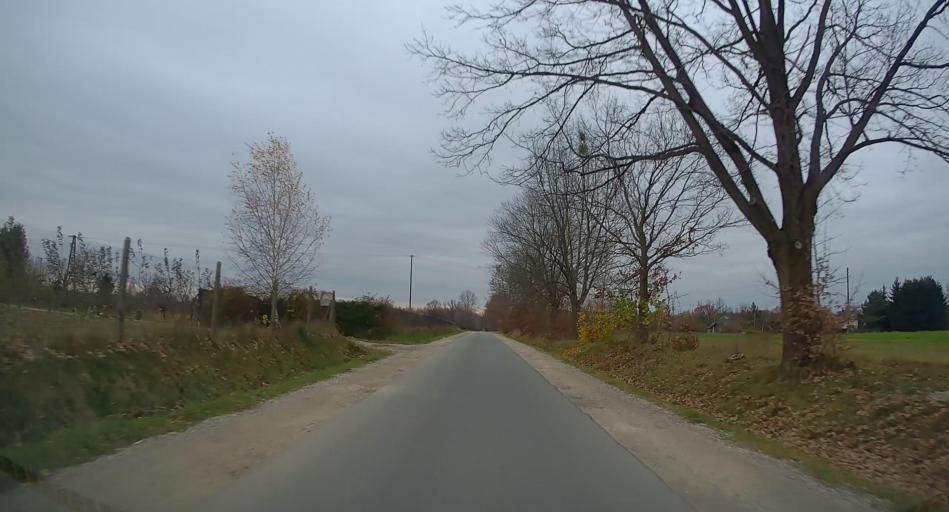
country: PL
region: Lodz Voivodeship
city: Zabia Wola
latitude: 52.0055
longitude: 20.6567
